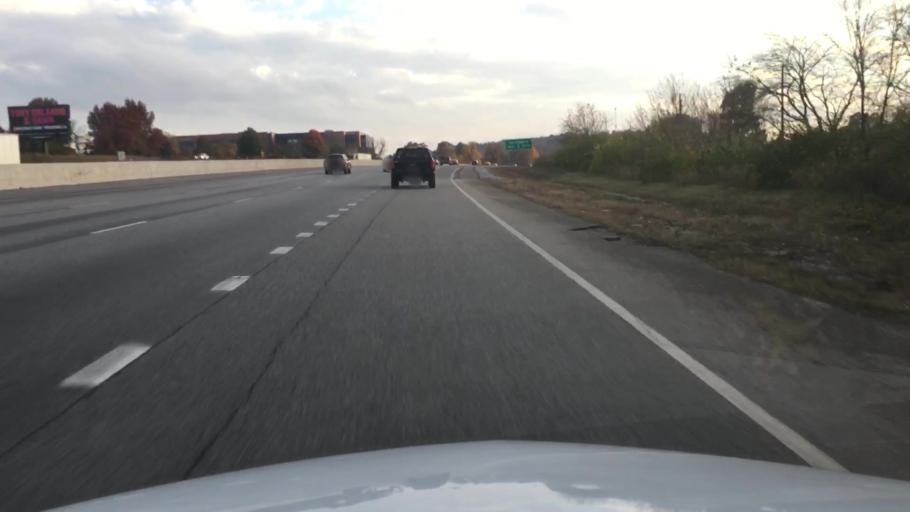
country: US
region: Arkansas
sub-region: Benton County
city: Lowell
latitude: 36.2493
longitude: -94.1507
